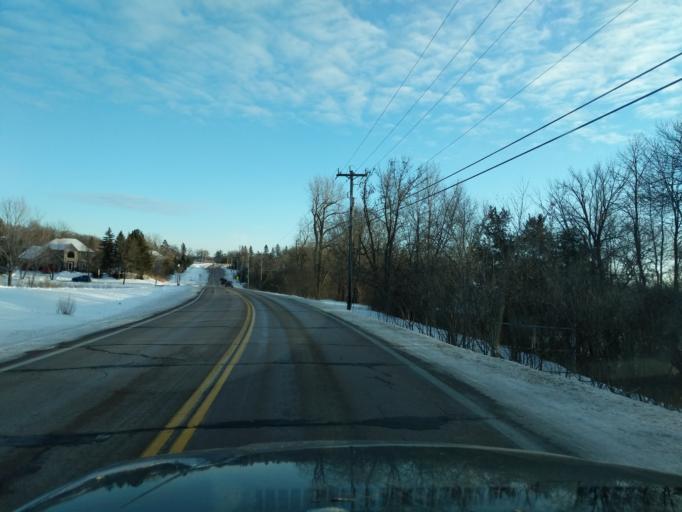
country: US
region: Minnesota
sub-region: Carver County
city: Victoria
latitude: 44.8741
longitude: -93.6410
